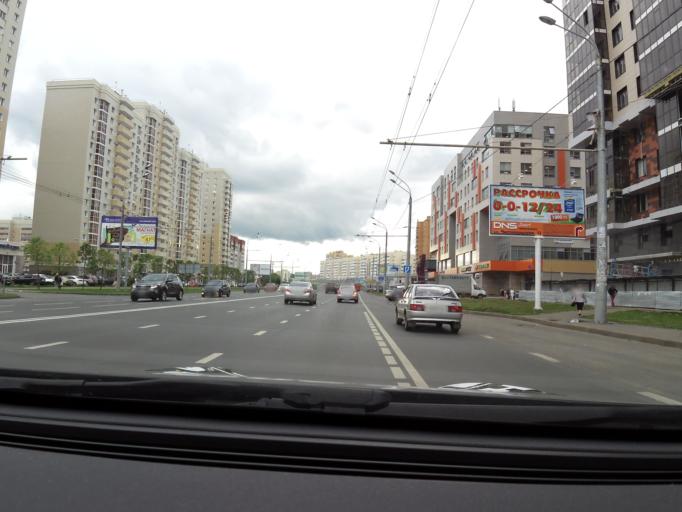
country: RU
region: Tatarstan
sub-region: Gorod Kazan'
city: Kazan
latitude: 55.8195
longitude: 49.1094
